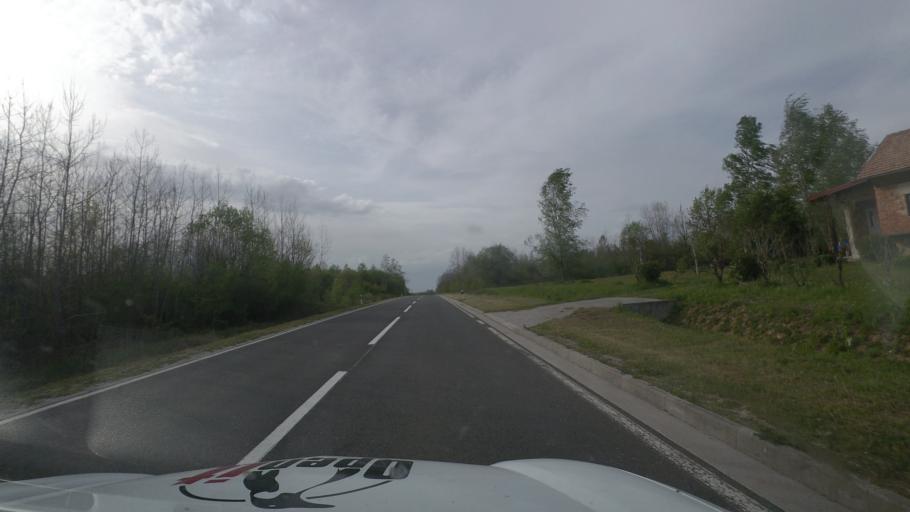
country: HR
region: Sisacko-Moslavacka
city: Gvozd
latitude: 45.3240
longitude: 15.9428
